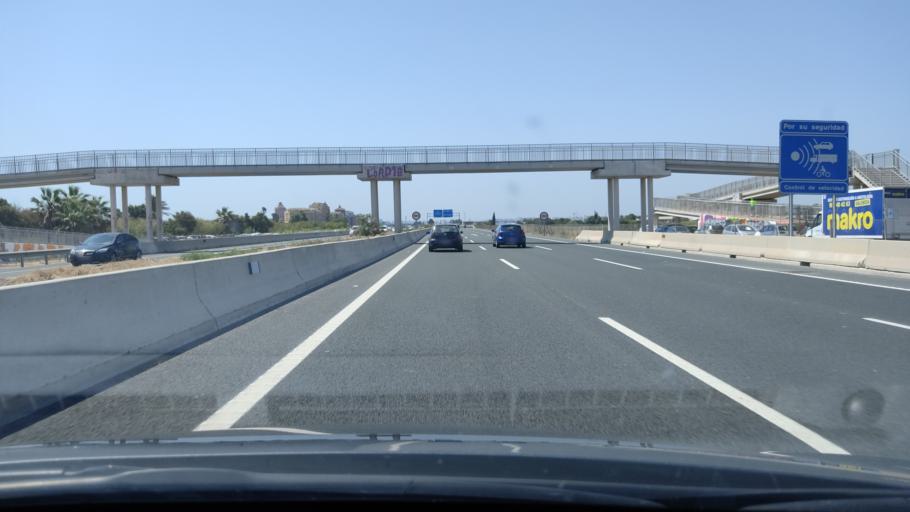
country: ES
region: Valencia
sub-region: Provincia de Valencia
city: Meliana
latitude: 39.5228
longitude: -0.3169
